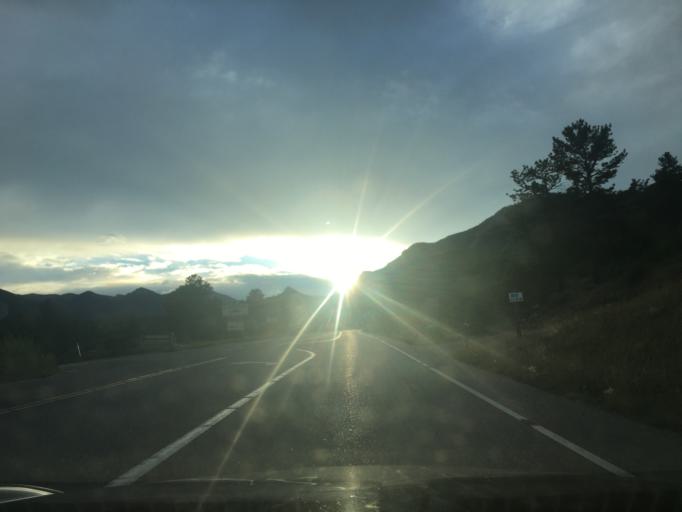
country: US
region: Colorado
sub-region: Larimer County
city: Estes Park
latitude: 40.4021
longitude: -105.5856
